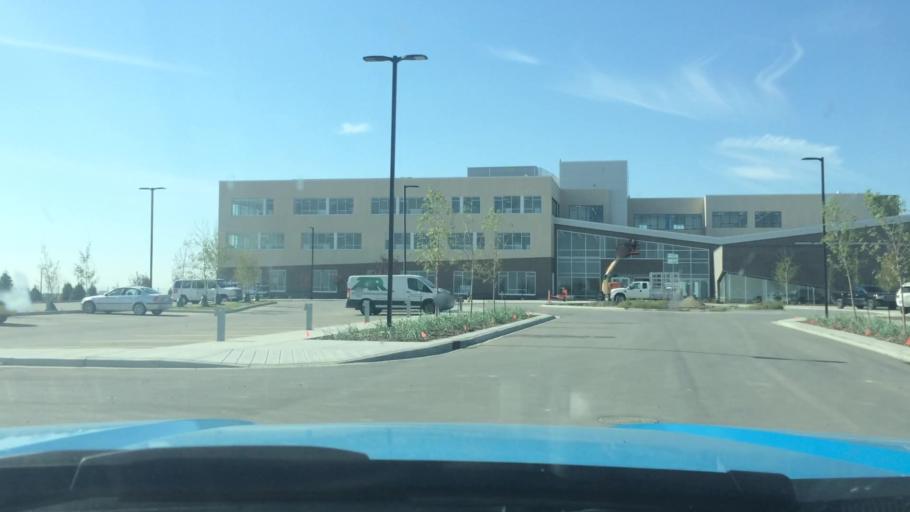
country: CA
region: Alberta
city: Airdrie
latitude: 51.2171
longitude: -113.9396
